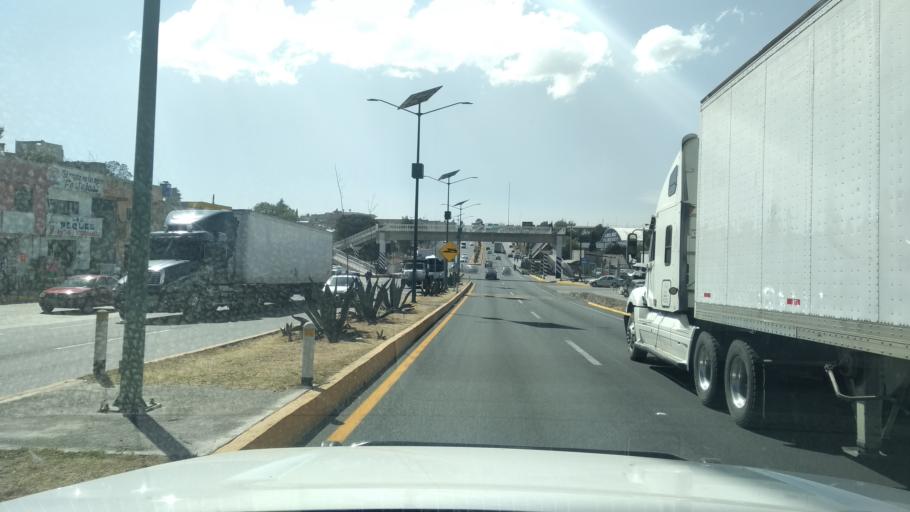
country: MX
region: Hidalgo
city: Calpulalpan
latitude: 19.5924
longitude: -98.5702
